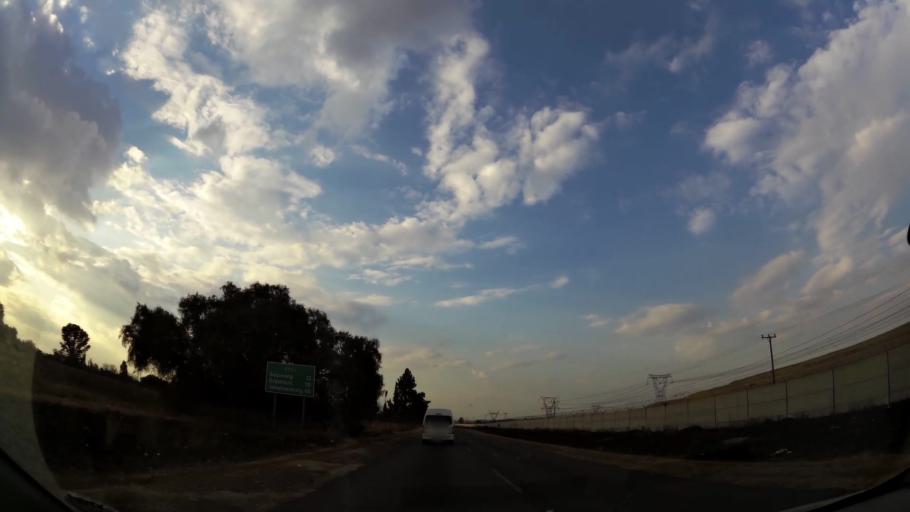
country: ZA
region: Gauteng
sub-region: Sedibeng District Municipality
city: Vanderbijlpark
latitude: -26.6377
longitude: 27.8067
